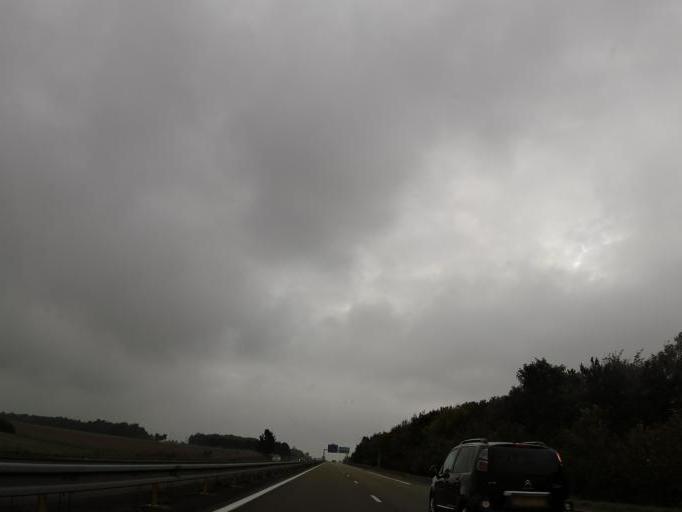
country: FR
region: Champagne-Ardenne
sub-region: Departement de la Marne
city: Fagnieres
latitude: 49.0454
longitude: 4.3134
